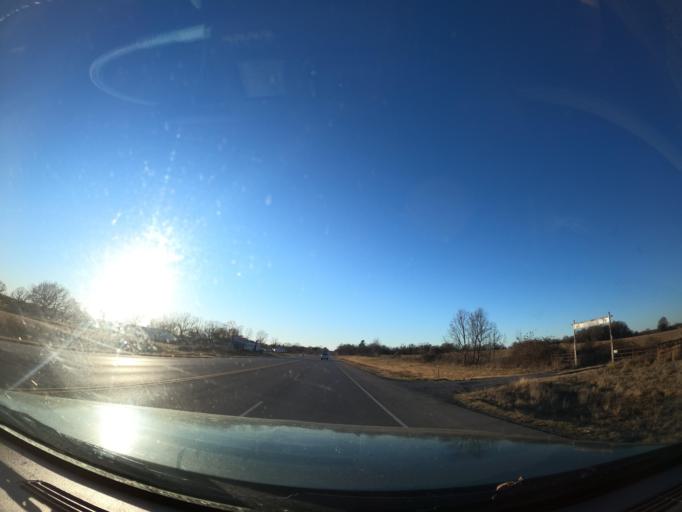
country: US
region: Oklahoma
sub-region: Pittsburg County
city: Krebs
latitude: 34.8941
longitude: -95.6358
